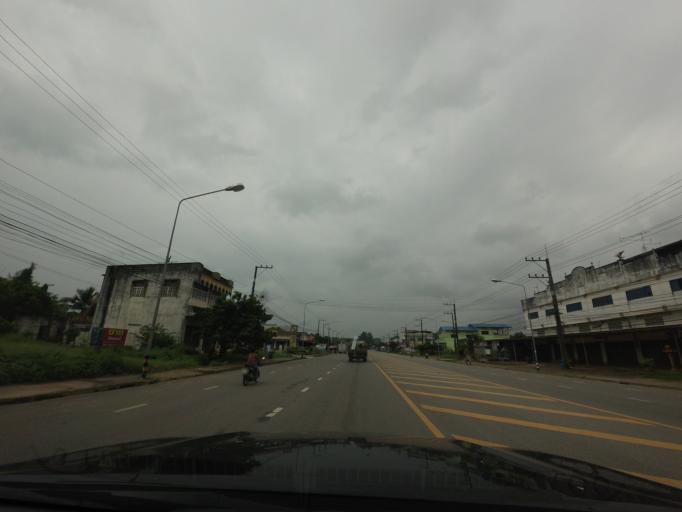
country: TH
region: Nong Khai
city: Si Chiang Mai
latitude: 17.9566
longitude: 102.5812
